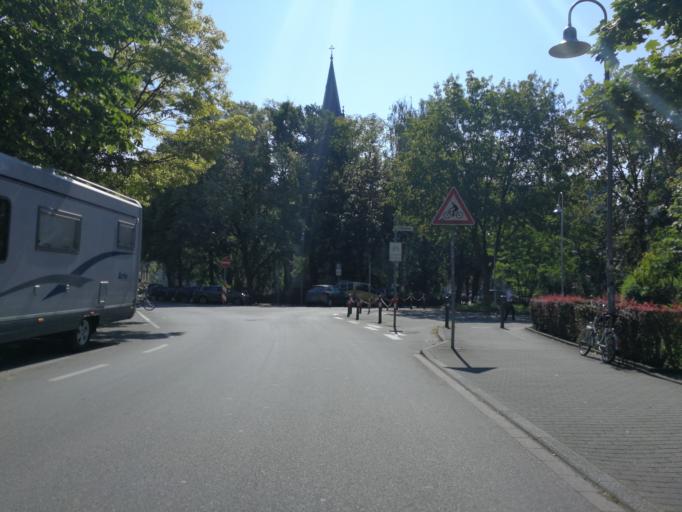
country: DE
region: Baden-Wuerttemberg
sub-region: Freiburg Region
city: Konstanz
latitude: 47.6618
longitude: 9.1702
